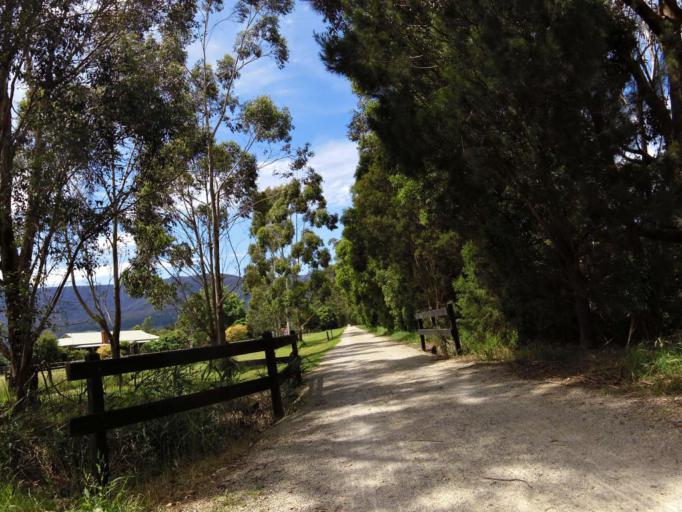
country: AU
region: Victoria
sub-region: Yarra Ranges
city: Yarra Junction
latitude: -37.7724
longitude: 145.6284
